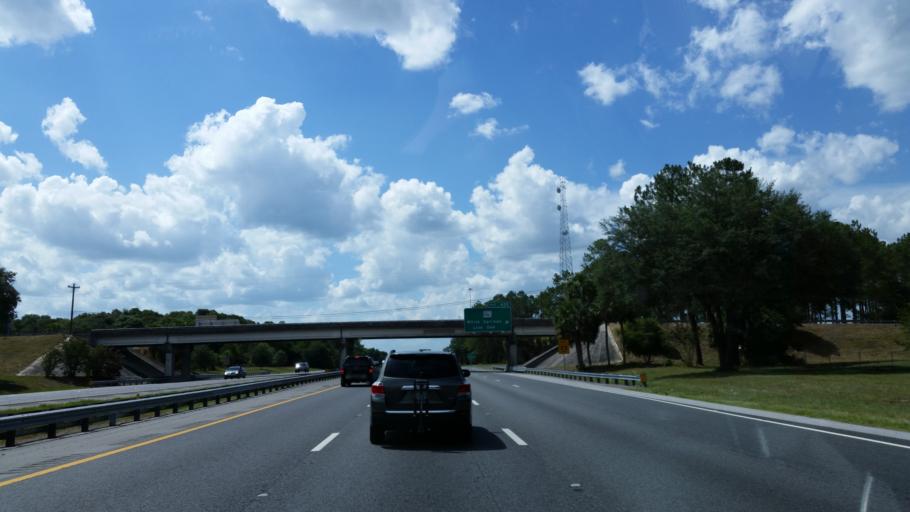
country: US
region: Florida
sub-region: Suwannee County
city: Wellborn
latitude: 30.3165
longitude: -82.8062
